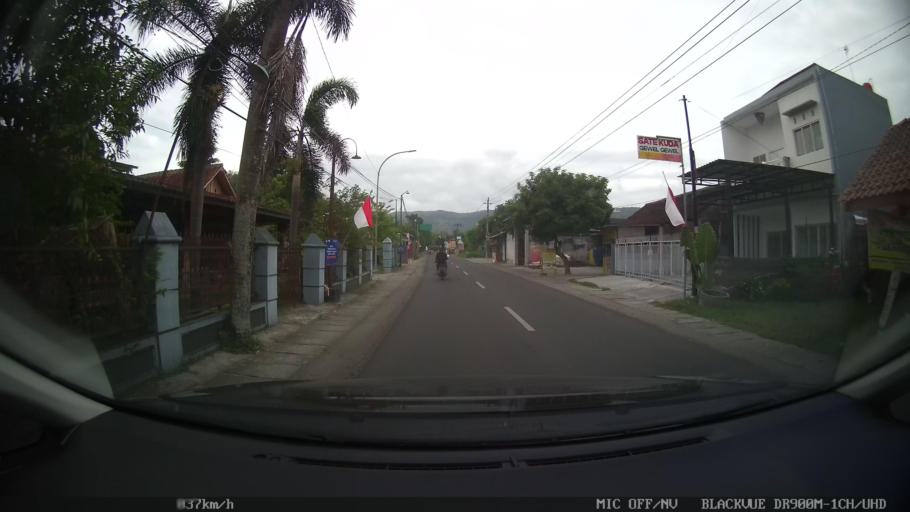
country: ID
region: Daerah Istimewa Yogyakarta
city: Sewon
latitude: -7.8795
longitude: 110.4169
